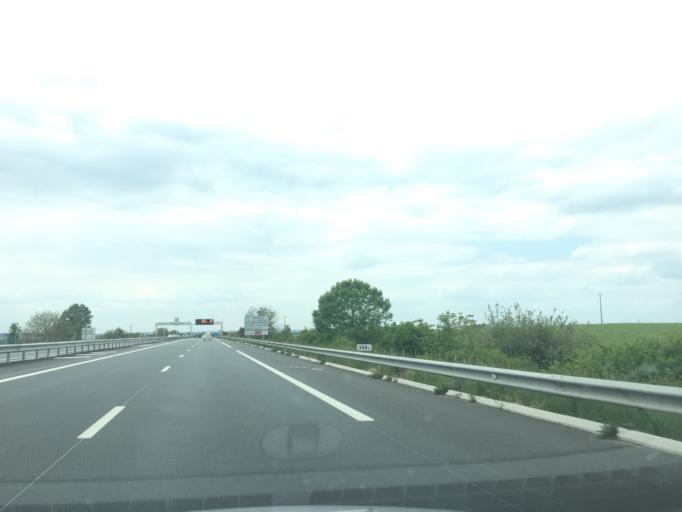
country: FR
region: Poitou-Charentes
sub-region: Departement des Deux-Sevres
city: Azay-le-Brule
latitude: 46.3671
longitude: -0.2417
